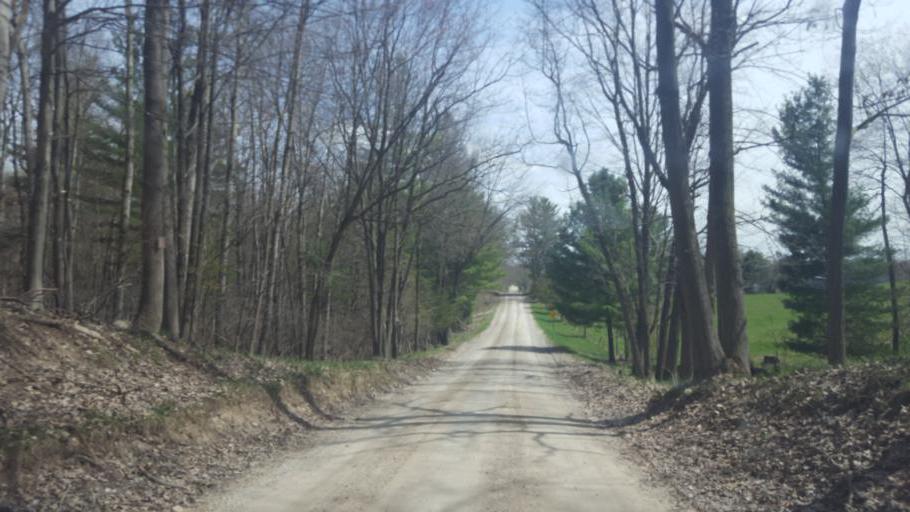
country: US
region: Michigan
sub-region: Isabella County
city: Lake Isabella
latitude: 43.5821
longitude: -84.9580
